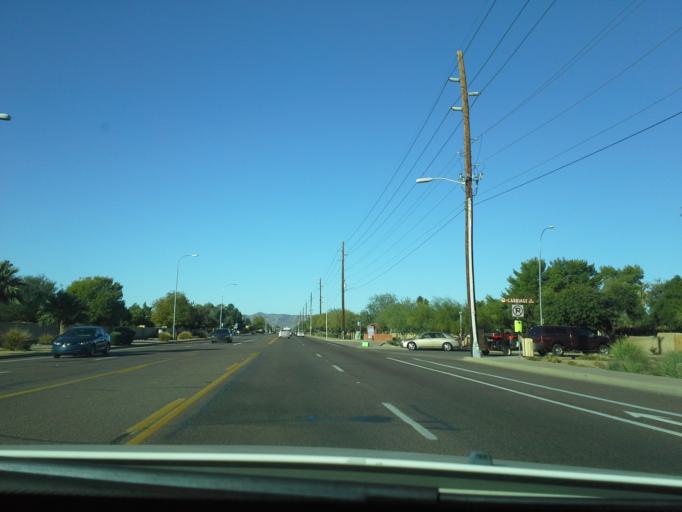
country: US
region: Arizona
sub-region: Maricopa County
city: San Carlos
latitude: 33.3495
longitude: -111.8807
